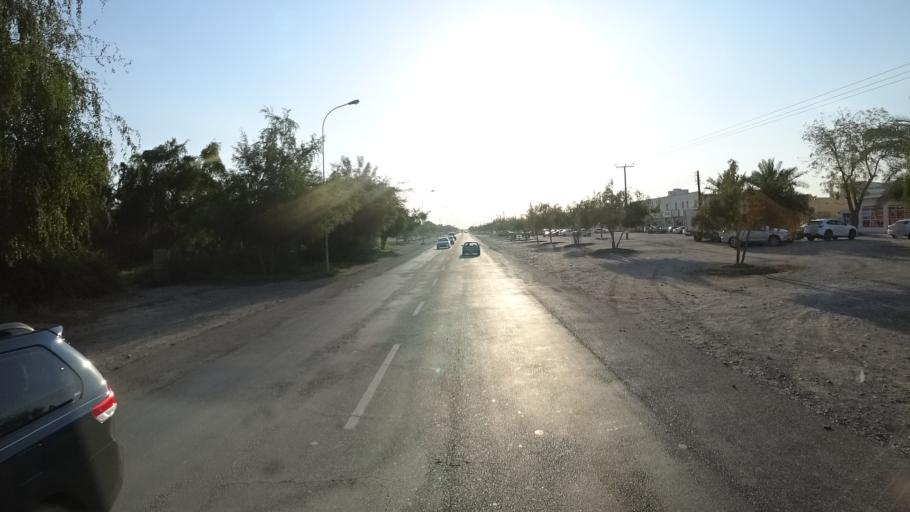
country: OM
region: Al Batinah
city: Al Khaburah
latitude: 23.9606
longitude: 57.0739
